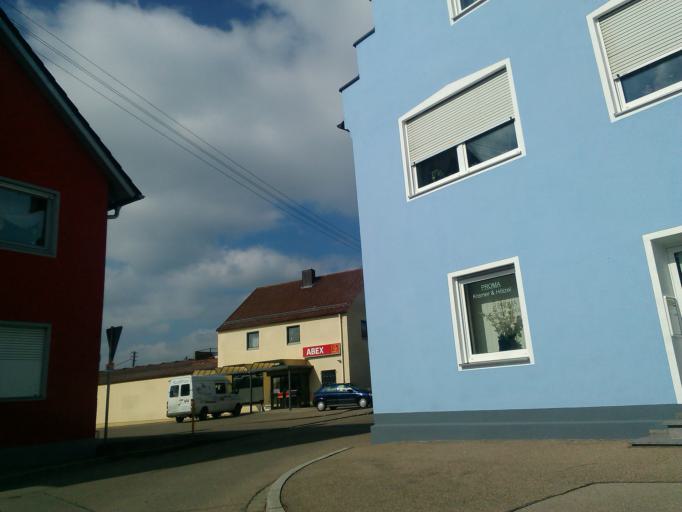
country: DE
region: Bavaria
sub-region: Swabia
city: Jettingen-Scheppach
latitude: 48.3906
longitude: 10.4358
